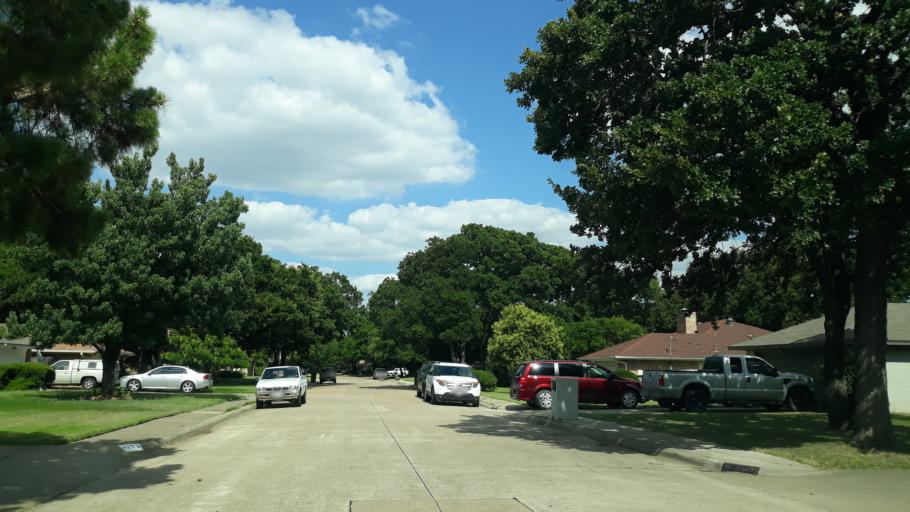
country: US
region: Texas
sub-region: Dallas County
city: Irving
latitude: 32.8130
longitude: -97.0010
